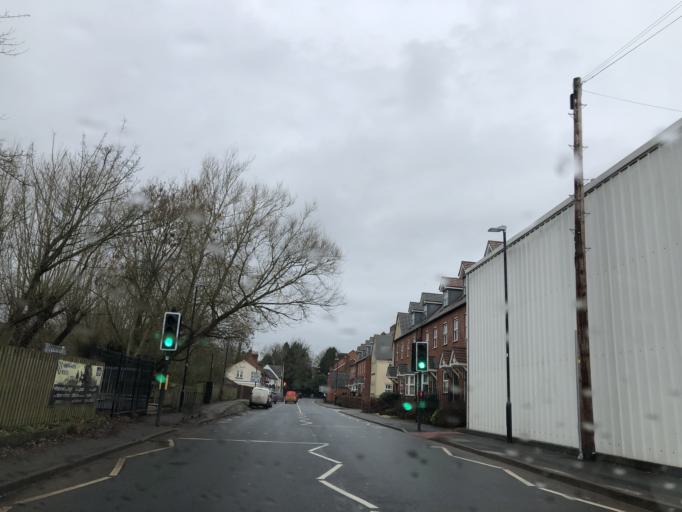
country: GB
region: England
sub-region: Warwickshire
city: Henley in Arden
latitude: 52.2875
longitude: -1.7782
